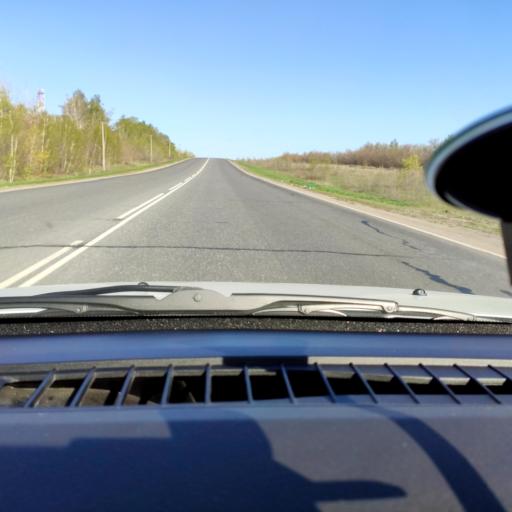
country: RU
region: Samara
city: Dubovyy Umet
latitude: 53.0744
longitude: 50.3570
